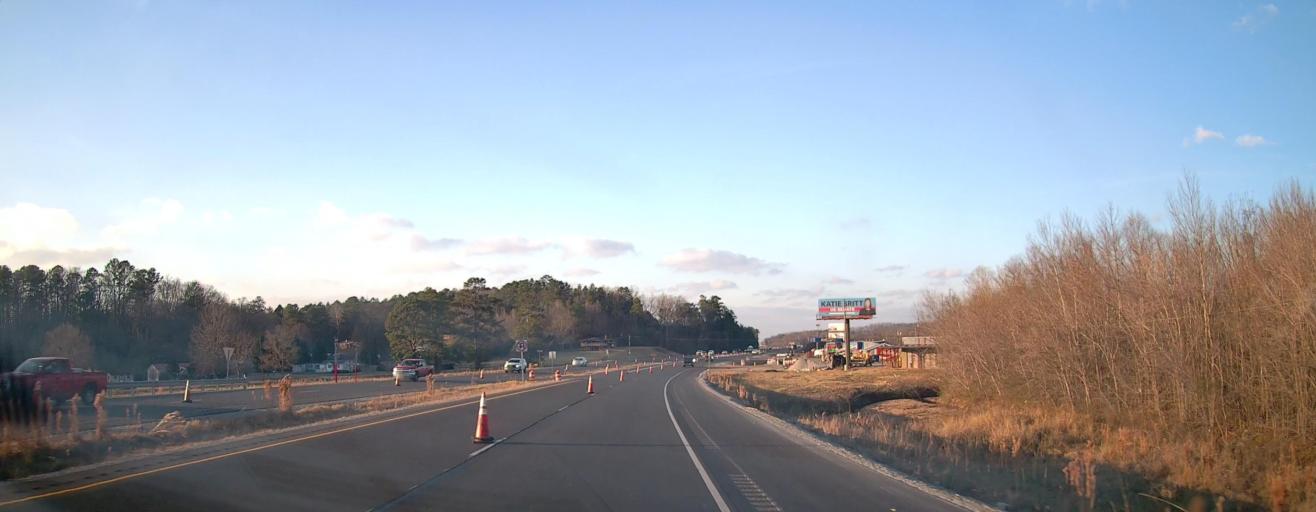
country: US
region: Alabama
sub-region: Calhoun County
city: Saks
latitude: 33.7233
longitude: -85.8762
